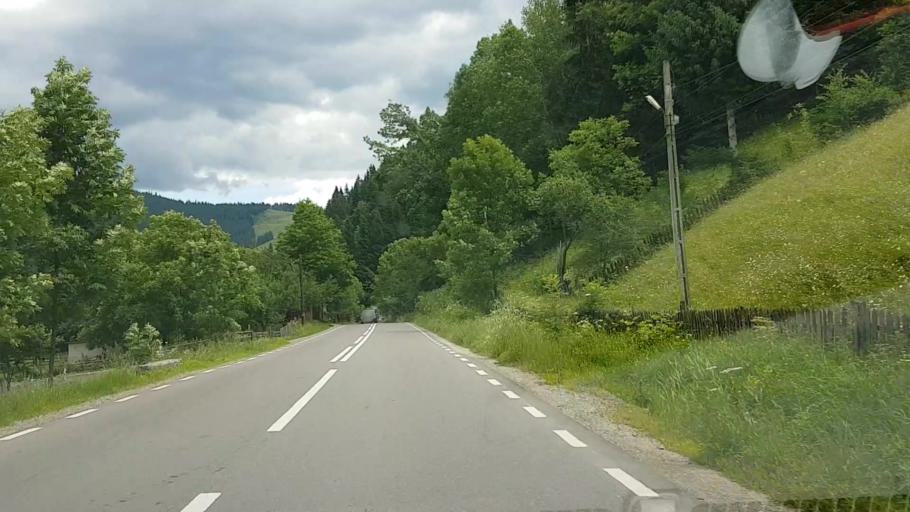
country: RO
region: Neamt
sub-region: Comuna Farcasa
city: Farcasa
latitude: 47.1351
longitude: 25.8768
